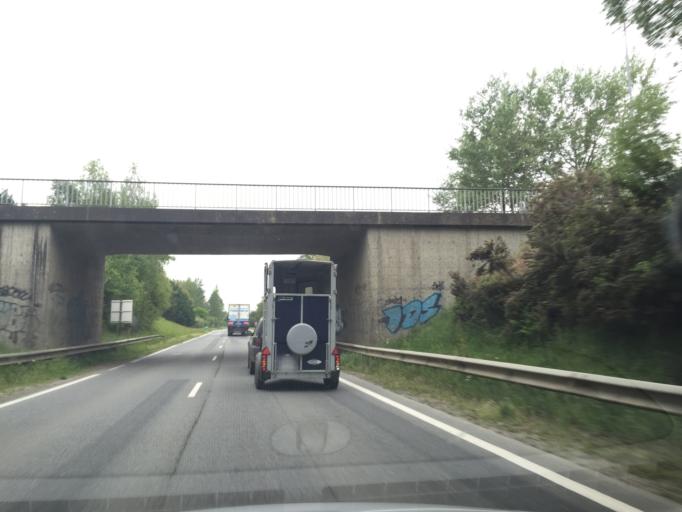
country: FR
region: Brittany
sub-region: Departement des Cotes-d'Armor
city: Lamballe
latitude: 48.4773
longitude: -2.5206
